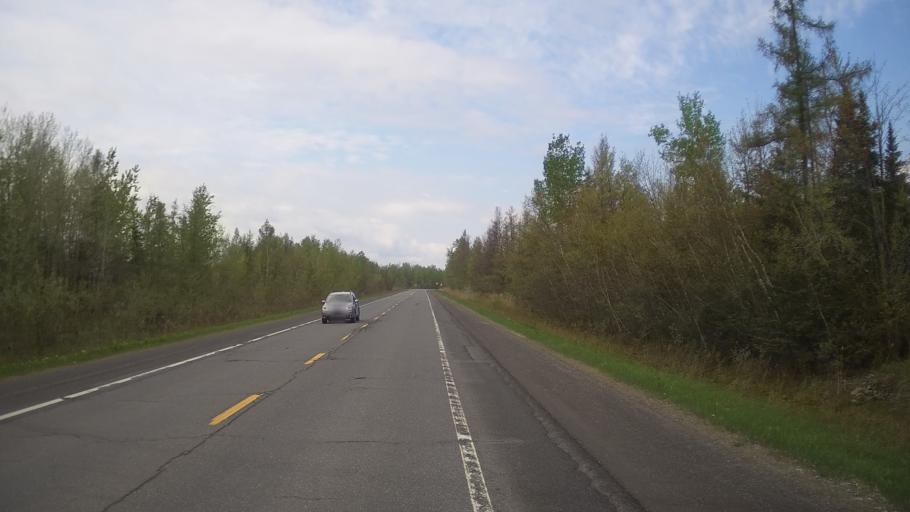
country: CA
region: Quebec
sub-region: Monteregie
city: Cowansville
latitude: 45.1935
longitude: -72.7367
